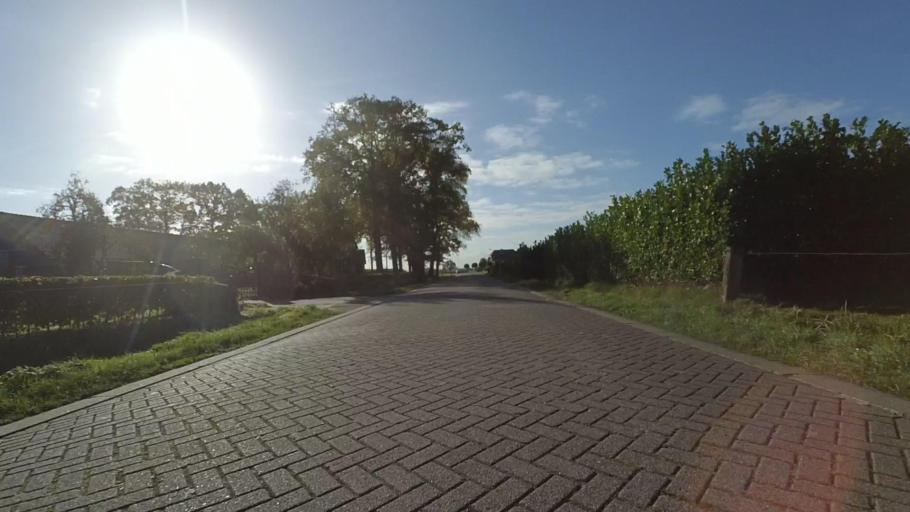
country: NL
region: Gelderland
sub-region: Gemeente Ermelo
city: Horst
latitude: 52.2726
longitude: 5.5547
